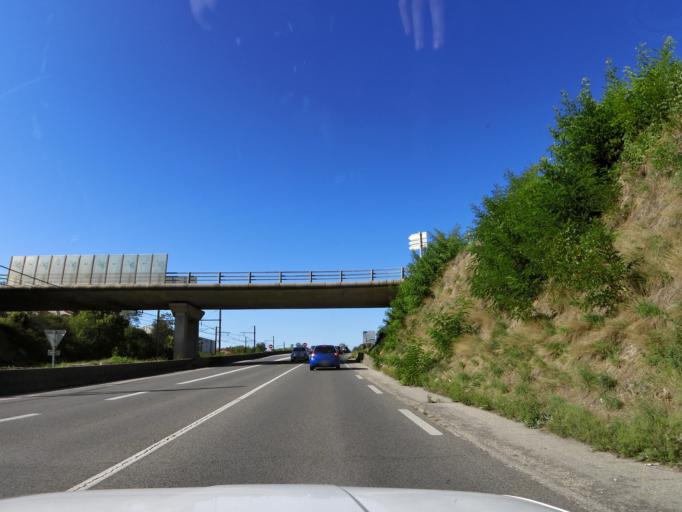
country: FR
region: Rhone-Alpes
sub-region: Departement de l'Ain
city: Amberieu-en-Bugey
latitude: 45.9711
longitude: 5.3471
